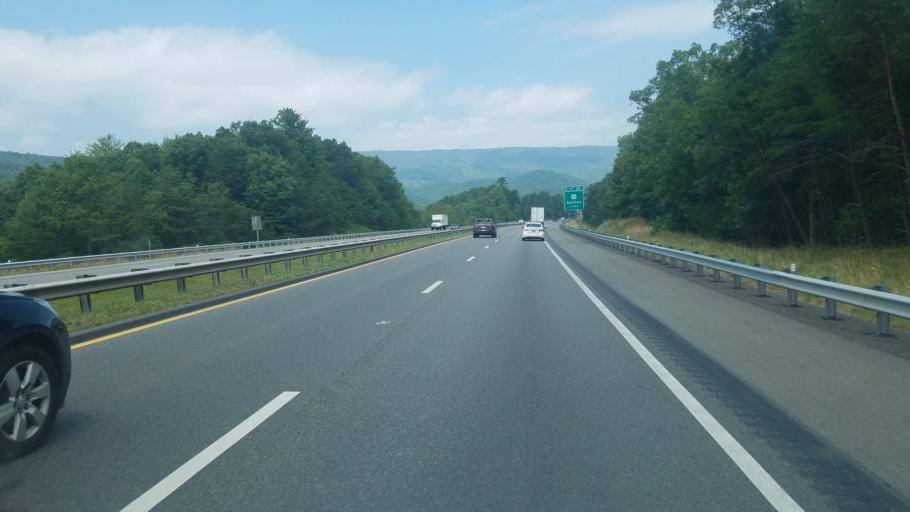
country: US
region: Virginia
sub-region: Bland County
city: Bland
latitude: 37.1566
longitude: -81.1419
